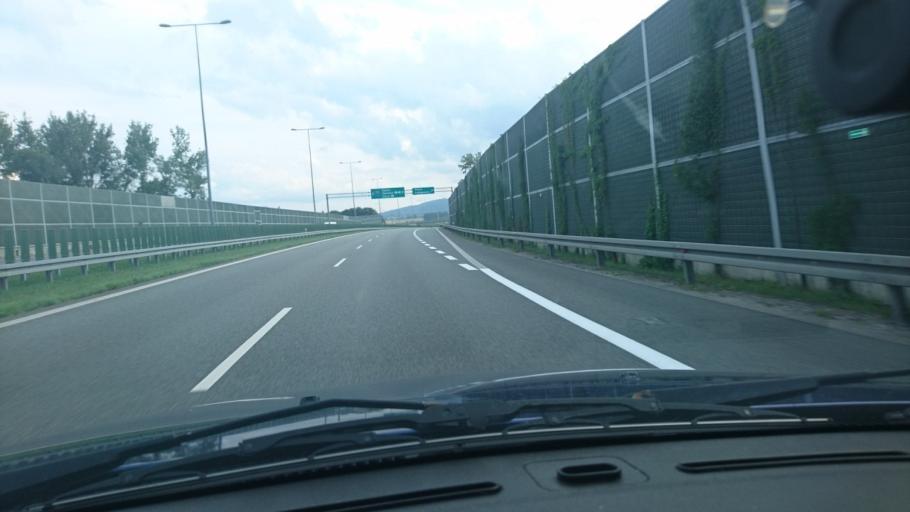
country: PL
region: Silesian Voivodeship
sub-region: Powiat zywiecki
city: Lodygowice
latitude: 49.7166
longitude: 19.1222
